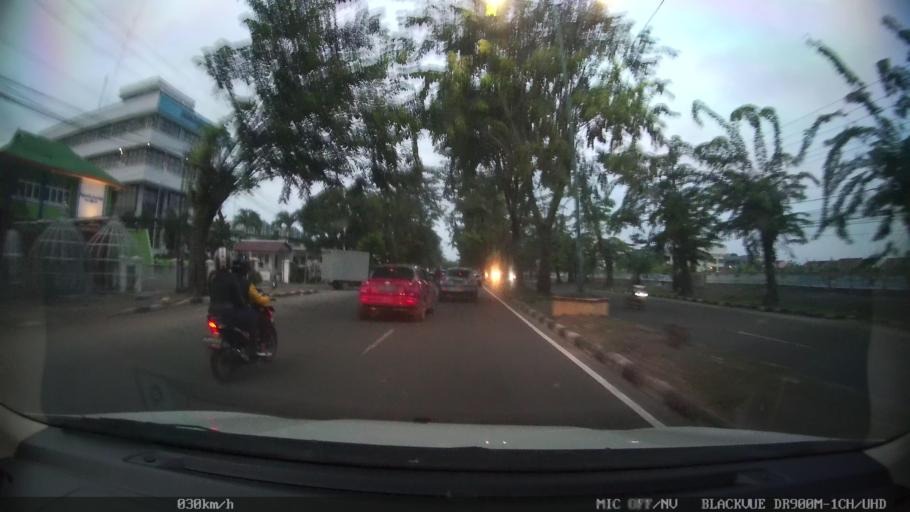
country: ID
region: North Sumatra
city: Sunggal
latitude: 3.5911
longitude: 98.6381
